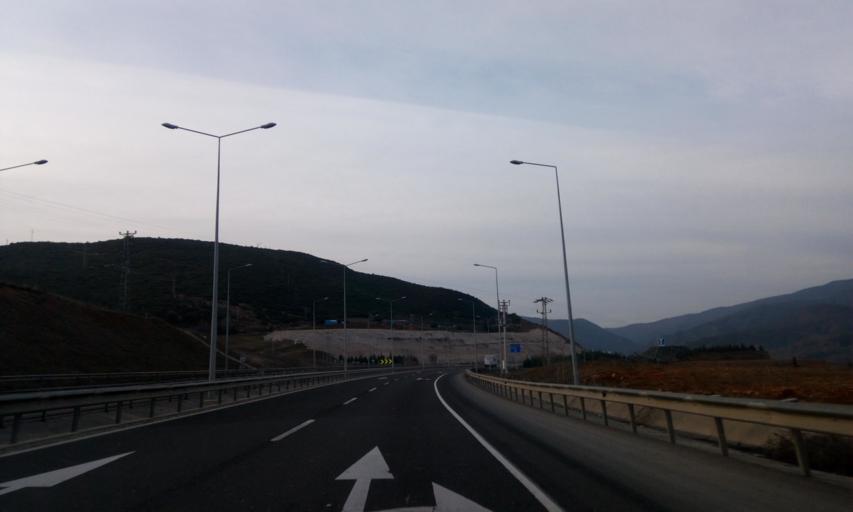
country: TR
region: Bilecik
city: Kuplu
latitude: 40.1242
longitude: 30.0140
